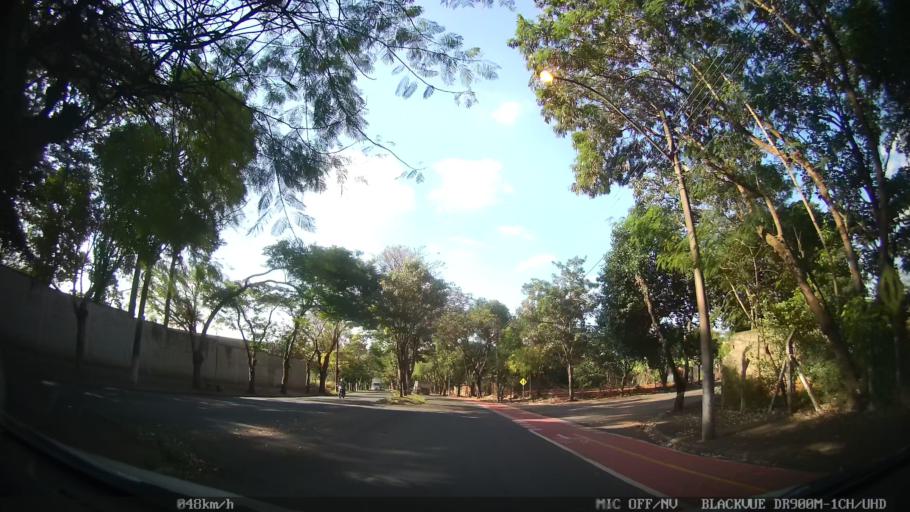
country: BR
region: Sao Paulo
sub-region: Nova Odessa
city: Nova Odessa
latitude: -22.7724
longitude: -47.3031
